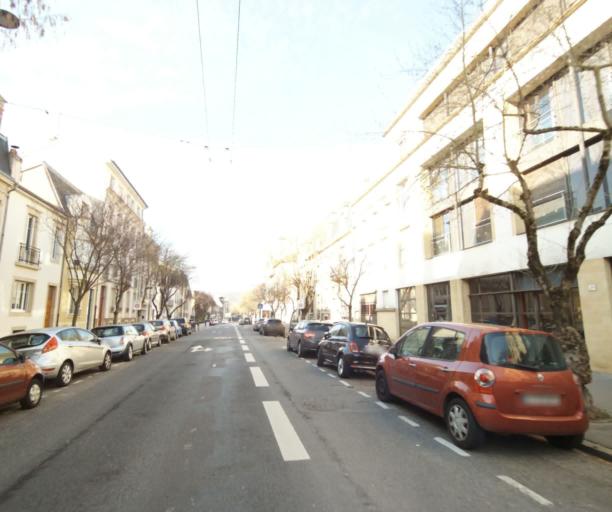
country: FR
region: Lorraine
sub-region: Departement de Meurthe-et-Moselle
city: Laxou
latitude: 48.6854
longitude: 6.1566
